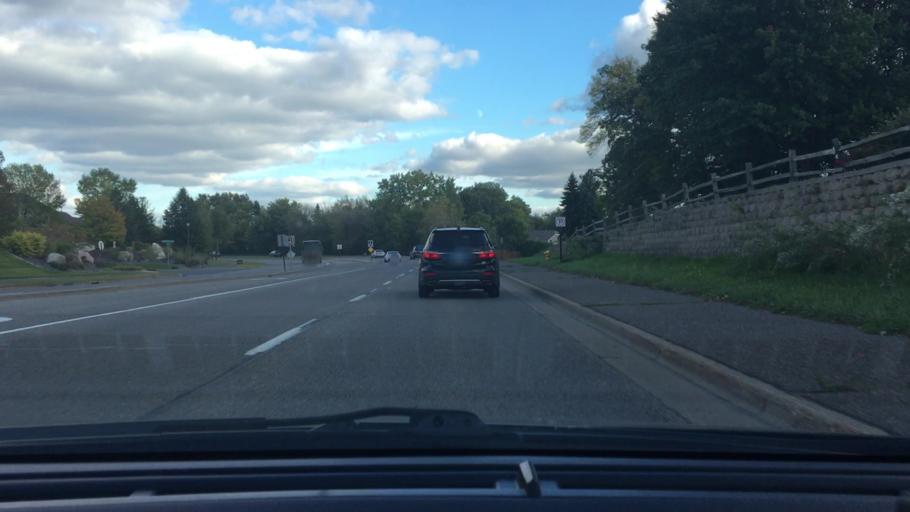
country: US
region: Minnesota
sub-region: Hennepin County
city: Maple Grove
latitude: 45.0593
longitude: -93.4295
